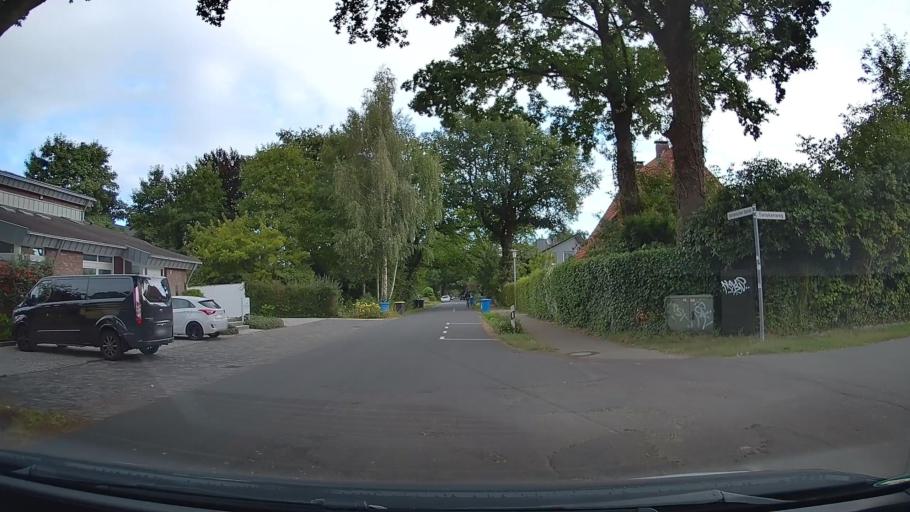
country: DE
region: Lower Saxony
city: Oldenburg
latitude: 53.1452
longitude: 8.1643
